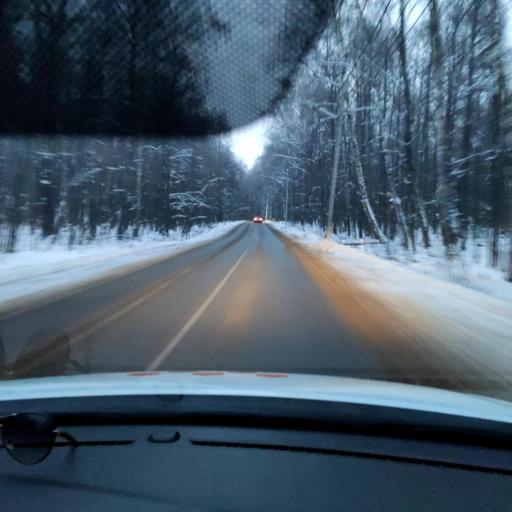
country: RU
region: Tatarstan
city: Vysokaya Gora
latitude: 55.9323
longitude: 49.1873
